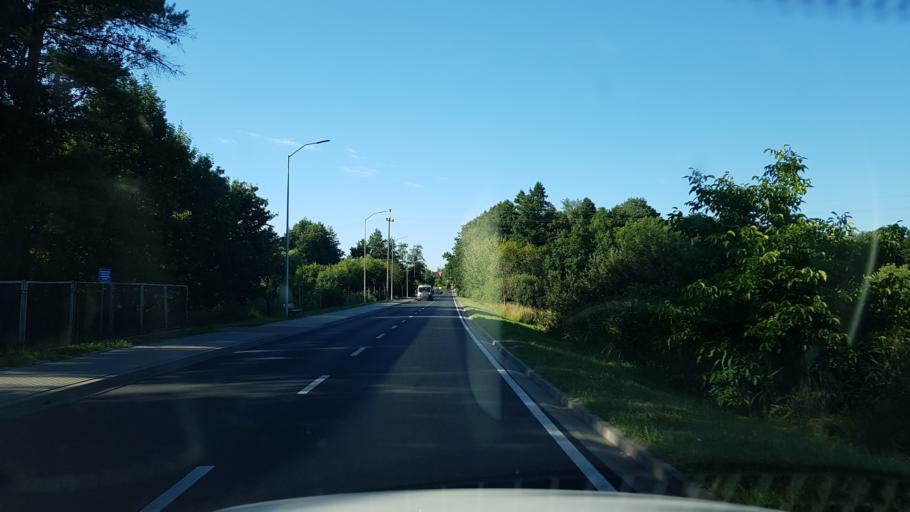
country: PL
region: West Pomeranian Voivodeship
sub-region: Powiat gryfinski
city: Chojna
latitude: 52.9543
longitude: 14.4401
